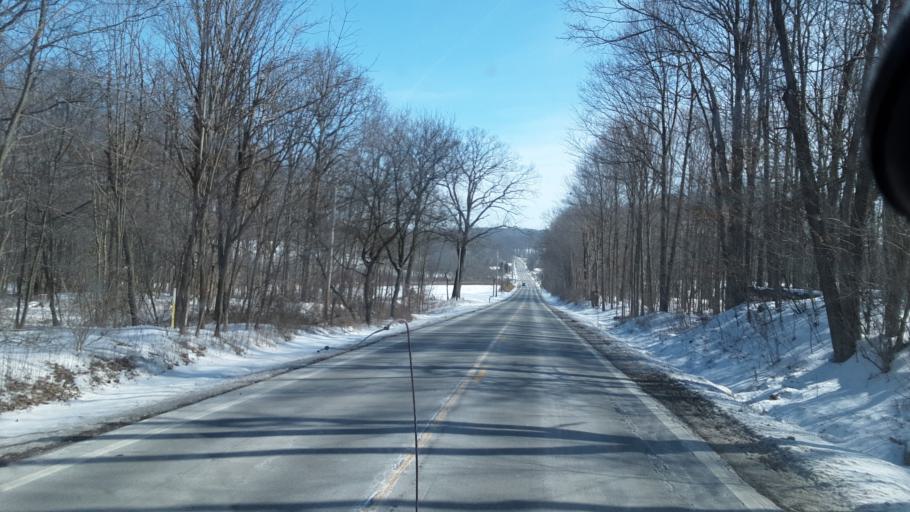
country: US
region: Ohio
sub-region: Mahoning County
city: Sebring
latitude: 40.9481
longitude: -80.9512
